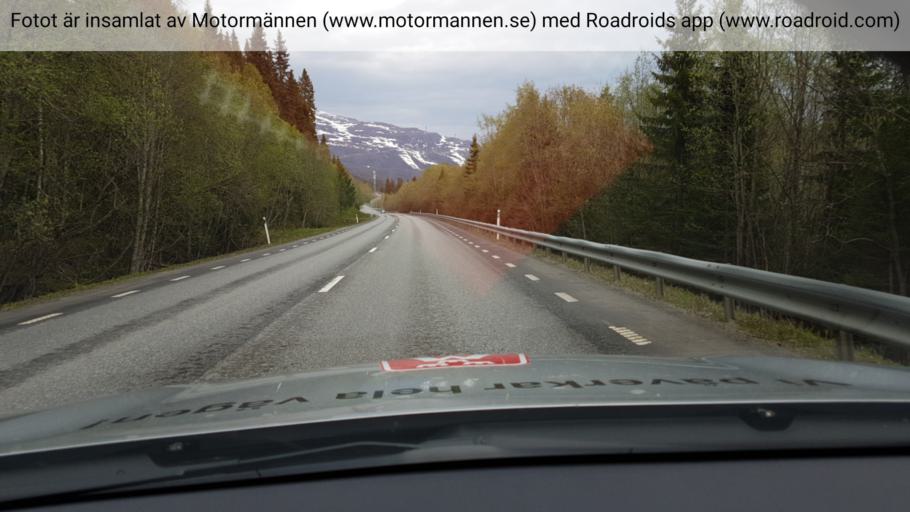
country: SE
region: Jaemtland
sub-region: Are Kommun
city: Are
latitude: 63.3969
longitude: 12.9650
